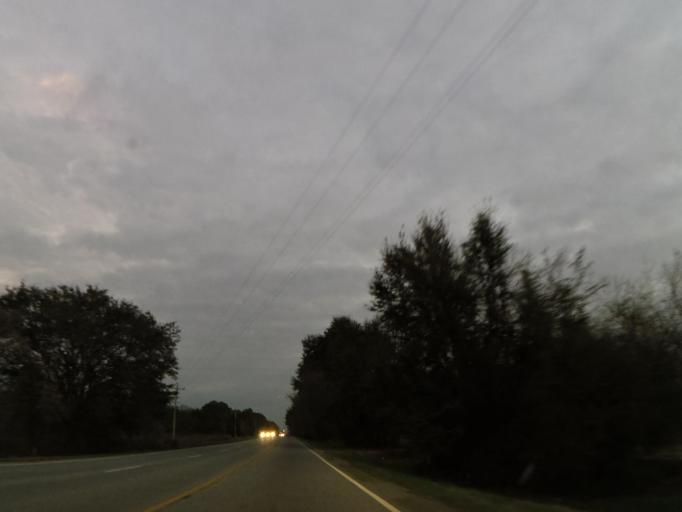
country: US
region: Georgia
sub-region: Dougherty County
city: Putney
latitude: 31.4325
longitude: -83.9676
